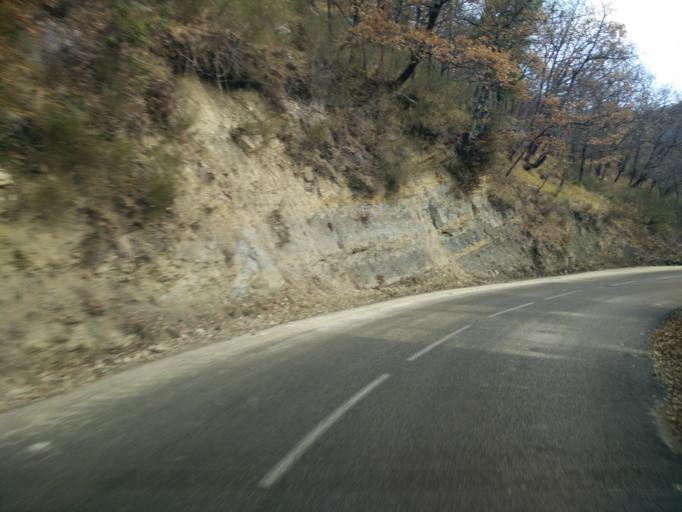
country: FR
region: Provence-Alpes-Cote d'Azur
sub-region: Departement des Alpes-Maritimes
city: Tourrettes-sur-Loup
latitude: 43.7956
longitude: 6.9849
